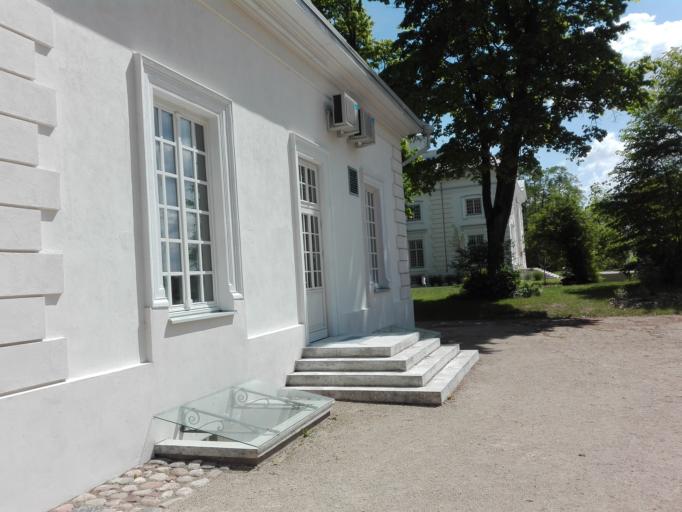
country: LT
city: Trakai
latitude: 54.6604
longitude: 24.9430
